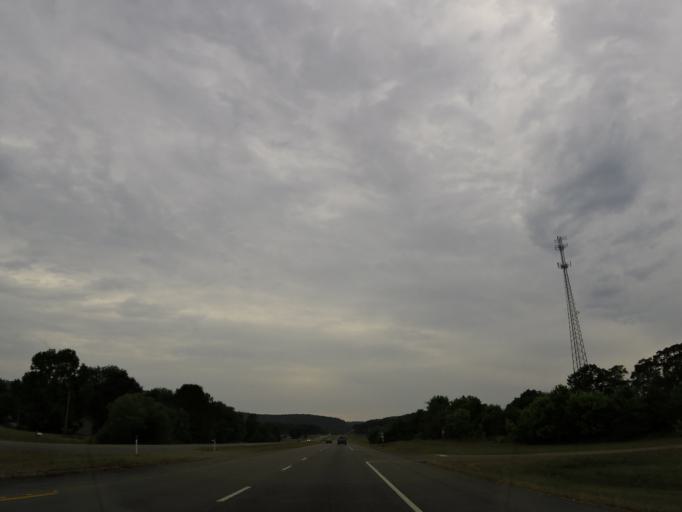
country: US
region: Alabama
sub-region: Jackson County
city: Scottsboro
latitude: 34.6213
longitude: -86.1610
